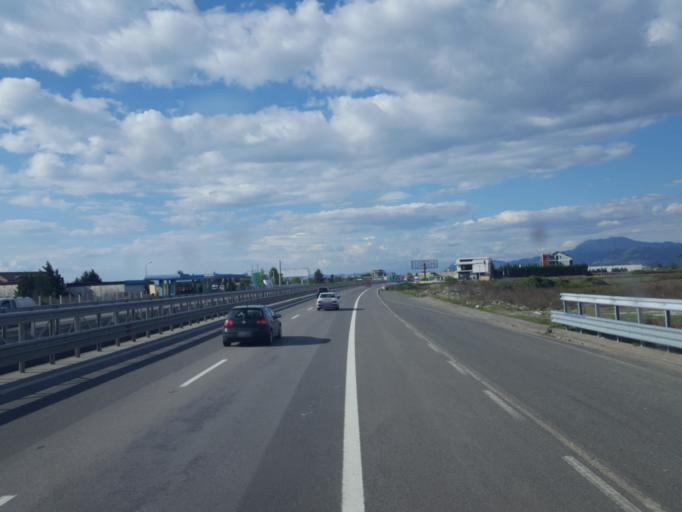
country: AL
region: Lezhe
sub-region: Rrethi i Kurbinit
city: Mamurras
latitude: 41.5972
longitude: 19.6685
